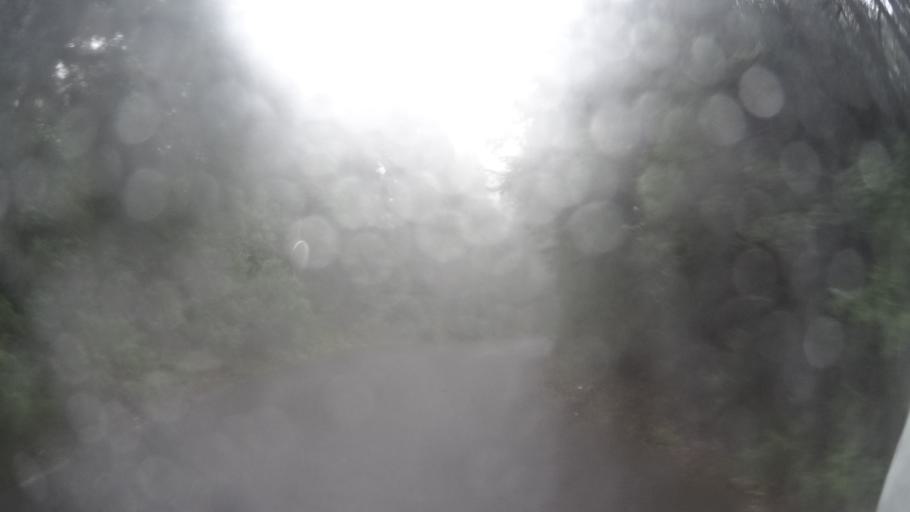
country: JP
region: Kagoshima
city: Nishinoomote
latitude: 30.2982
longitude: 130.5634
